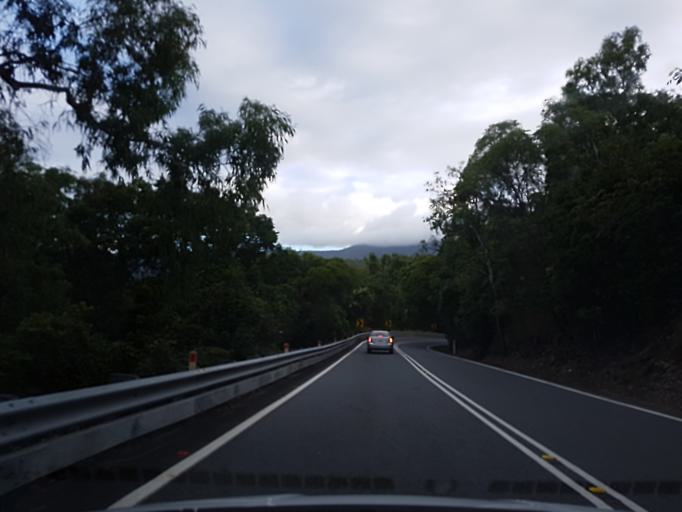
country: AU
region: Queensland
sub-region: Cairns
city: Palm Cove
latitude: -16.6519
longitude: 145.5648
